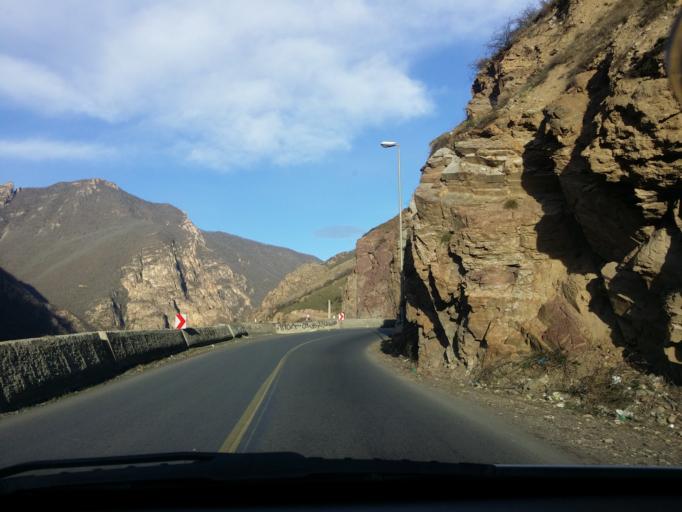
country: IR
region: Mazandaran
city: Chalus
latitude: 36.2634
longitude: 51.2645
